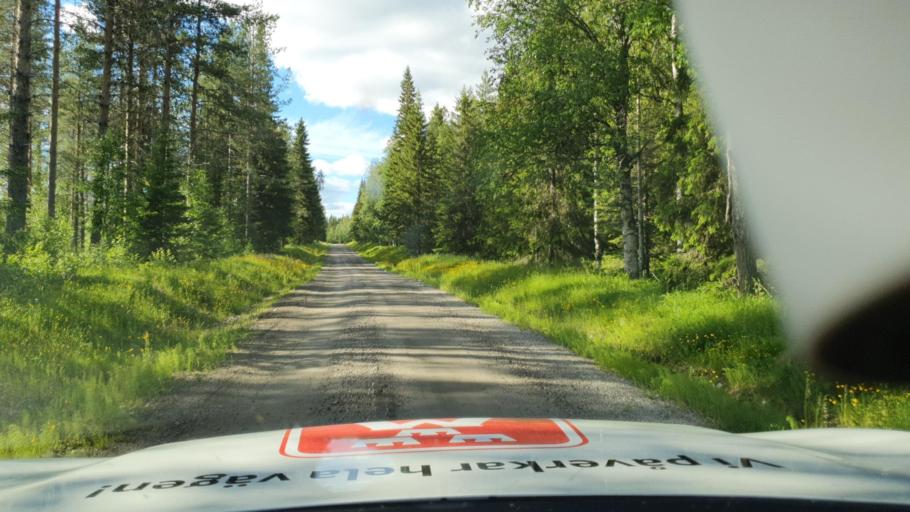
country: SE
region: Vaesterbotten
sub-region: Lycksele Kommun
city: Lycksele
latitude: 64.4080
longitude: 18.2911
